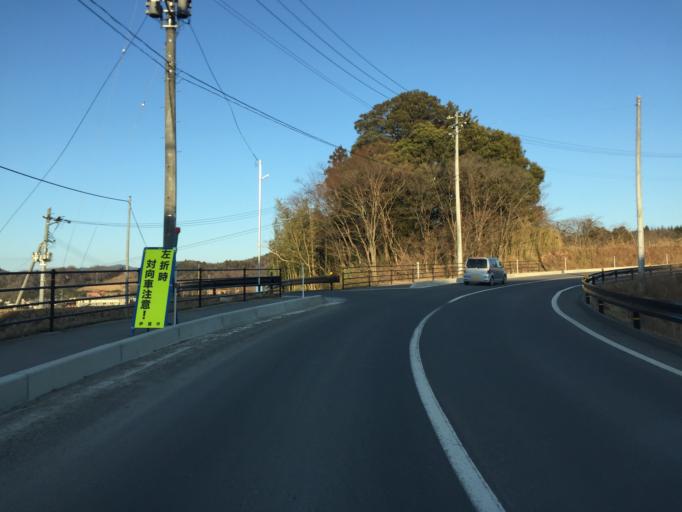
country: JP
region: Fukushima
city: Hobaramachi
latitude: 37.7670
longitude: 140.5901
